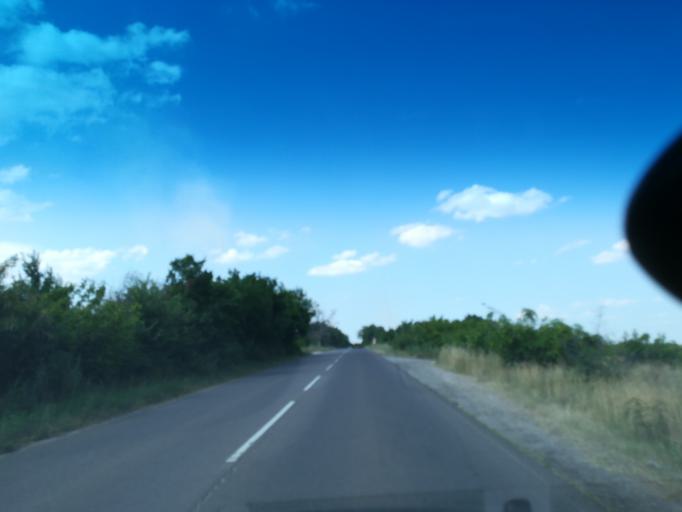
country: BG
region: Stara Zagora
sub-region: Obshtina Chirpan
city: Chirpan
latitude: 42.2116
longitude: 25.3663
